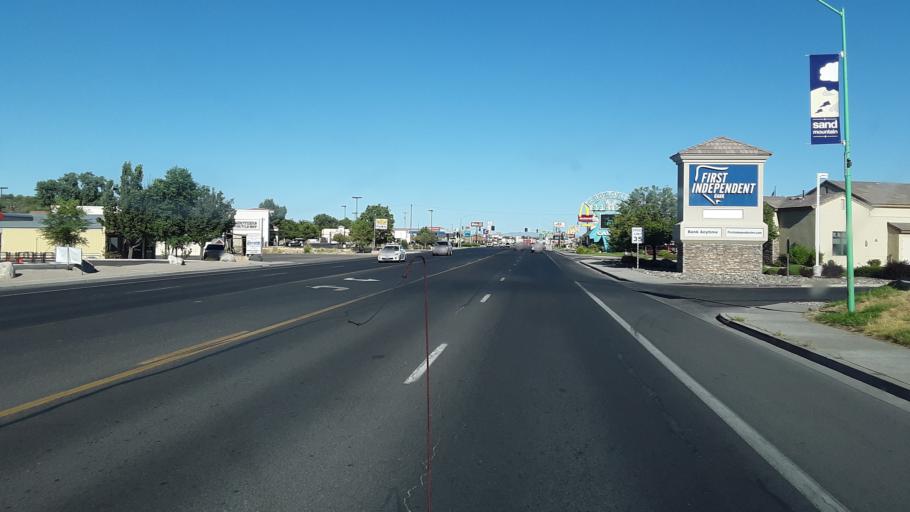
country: US
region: Nevada
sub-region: Churchill County
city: Fallon
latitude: 39.4769
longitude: -118.8030
